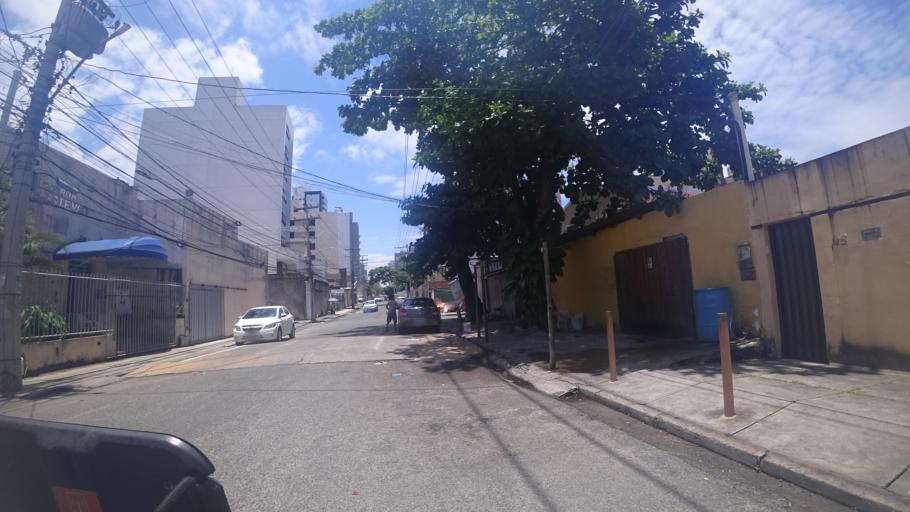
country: BR
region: Bahia
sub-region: Salvador
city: Salvador
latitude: -13.0097
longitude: -38.4676
